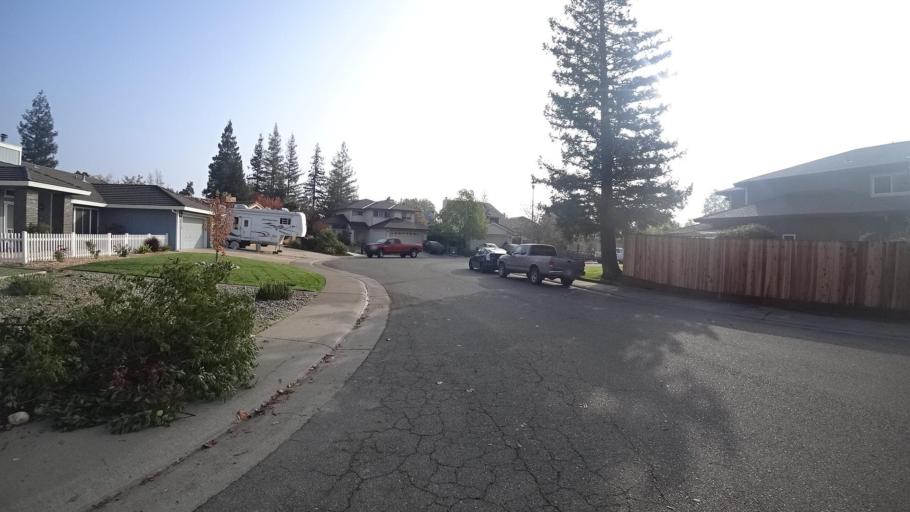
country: US
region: California
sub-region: Sacramento County
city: Elk Grove
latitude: 38.4108
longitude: -121.3553
